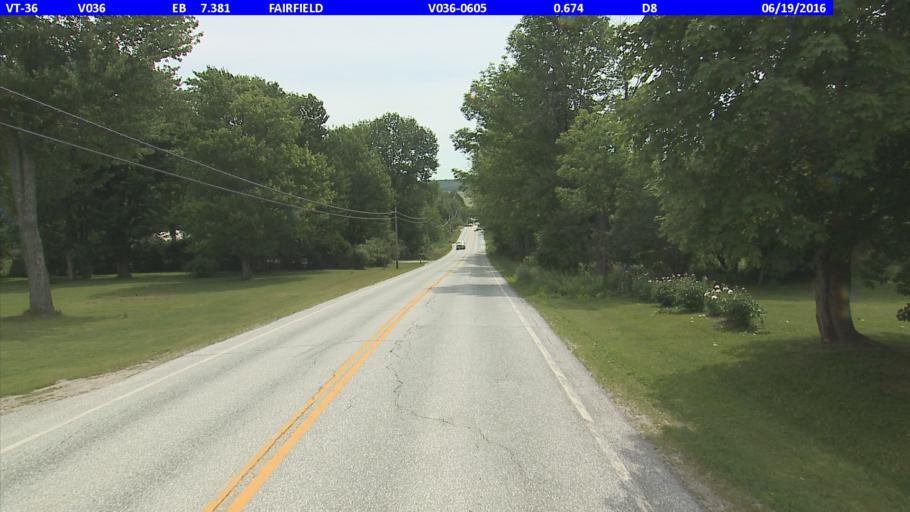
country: US
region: Vermont
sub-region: Franklin County
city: Saint Albans
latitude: 44.7887
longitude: -73.0183
